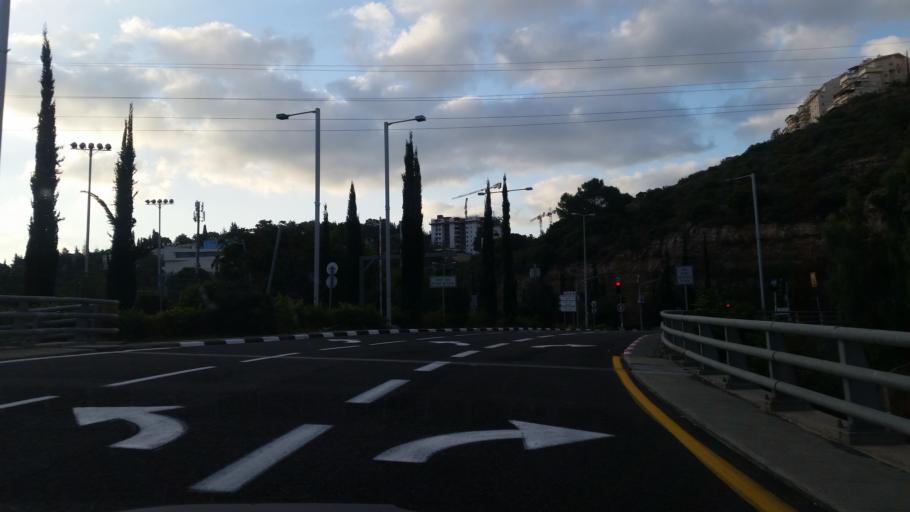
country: IL
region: Haifa
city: Haifa
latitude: 32.7899
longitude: 35.0093
